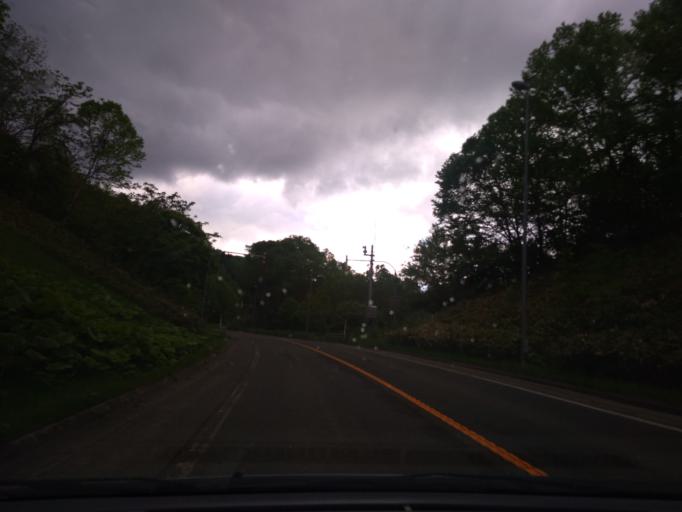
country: JP
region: Hokkaido
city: Shimo-furano
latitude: 43.0924
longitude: 142.4034
